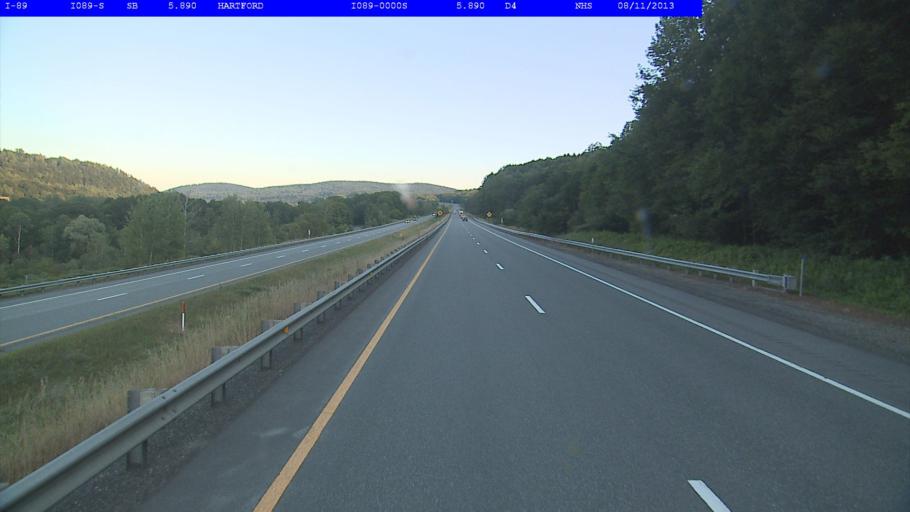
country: US
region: Vermont
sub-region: Windsor County
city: White River Junction
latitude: 43.6907
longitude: -72.4053
